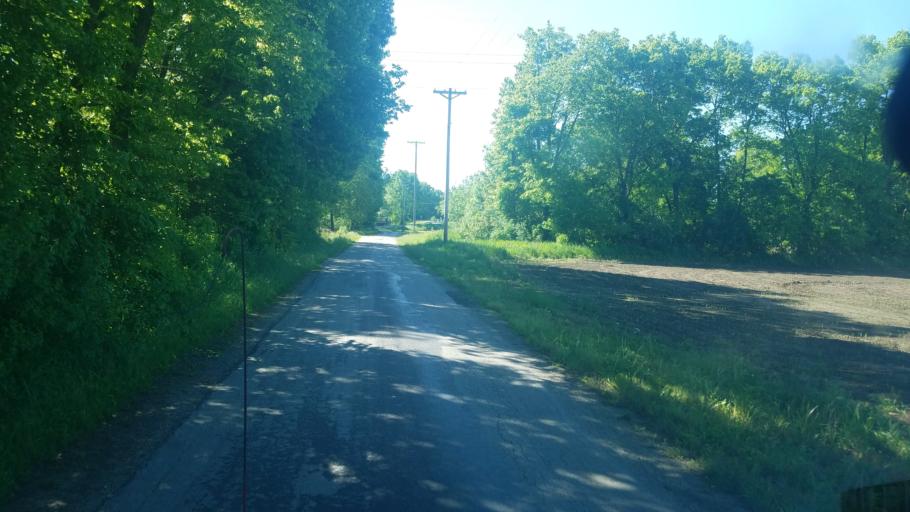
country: US
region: Ohio
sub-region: Marion County
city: Prospect
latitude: 40.5323
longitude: -83.2140
